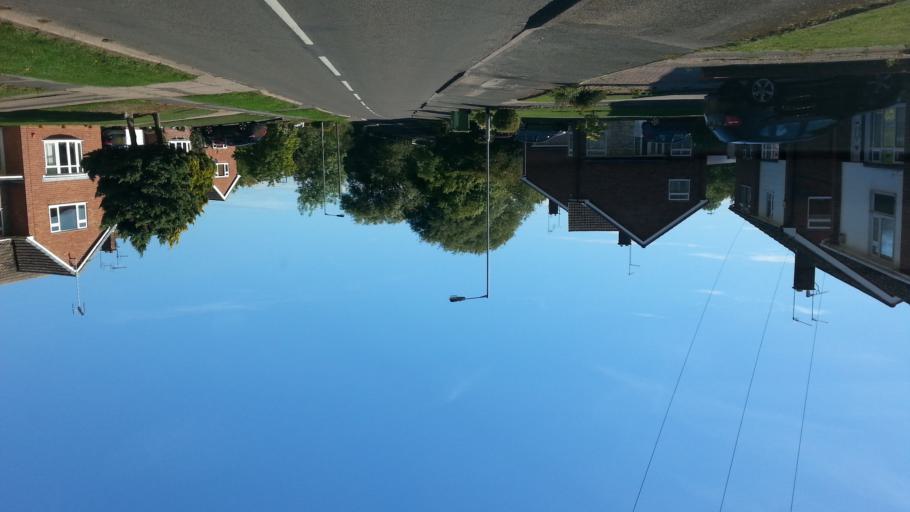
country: GB
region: England
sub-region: Staffordshire
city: Stafford
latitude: 52.8112
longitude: -2.1503
